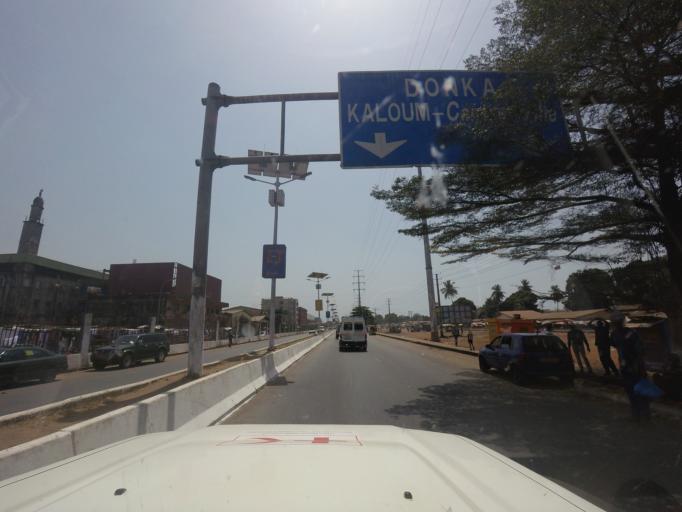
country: GN
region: Conakry
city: Conakry
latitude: 9.5470
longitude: -13.6660
